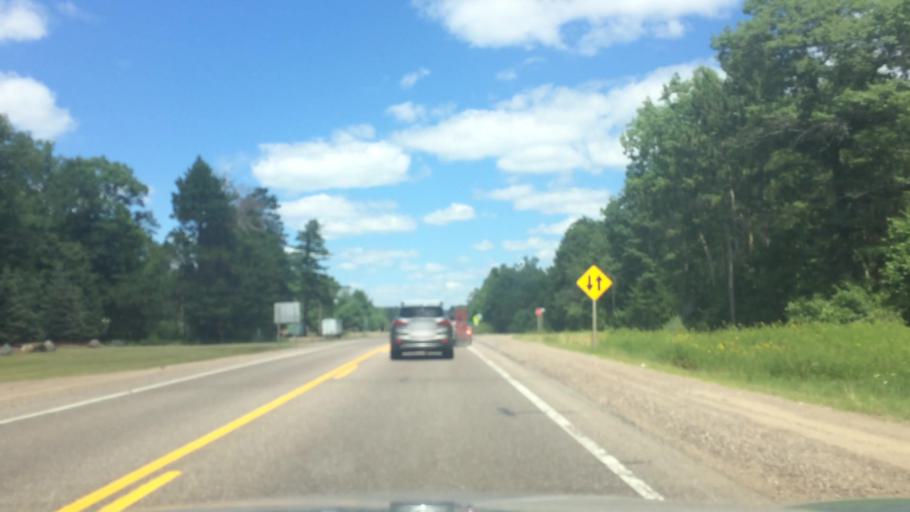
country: US
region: Wisconsin
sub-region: Vilas County
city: Lac du Flambeau
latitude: 45.9227
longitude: -89.6956
